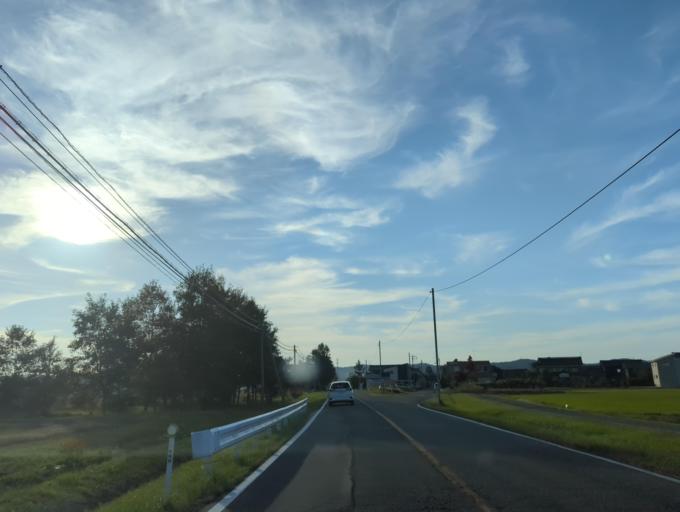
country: JP
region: Niigata
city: Mitsuke
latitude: 37.5552
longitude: 138.8393
